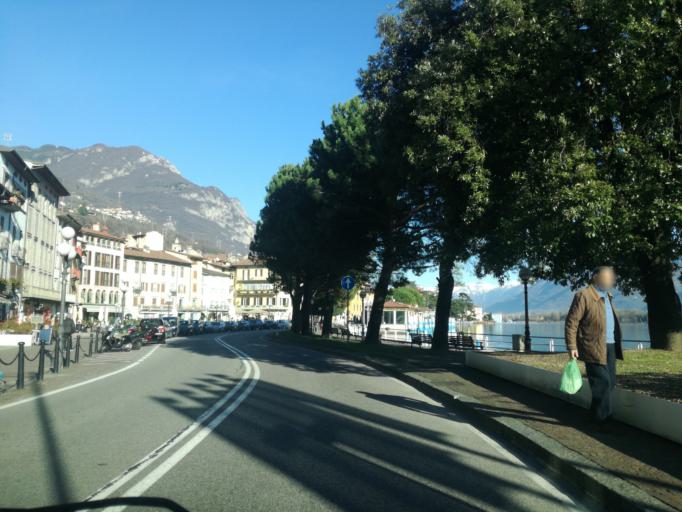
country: IT
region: Lombardy
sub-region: Provincia di Bergamo
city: Lovere
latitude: 45.8160
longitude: 10.0746
